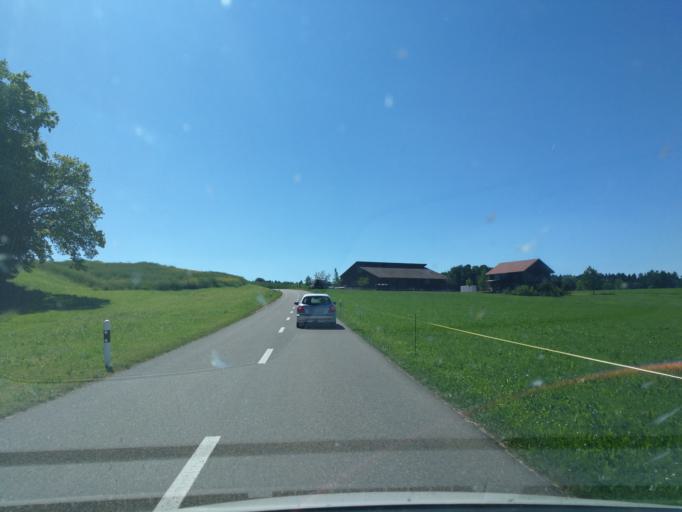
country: CH
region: Thurgau
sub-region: Weinfelden District
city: Sulgen
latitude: 47.5102
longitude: 9.1682
